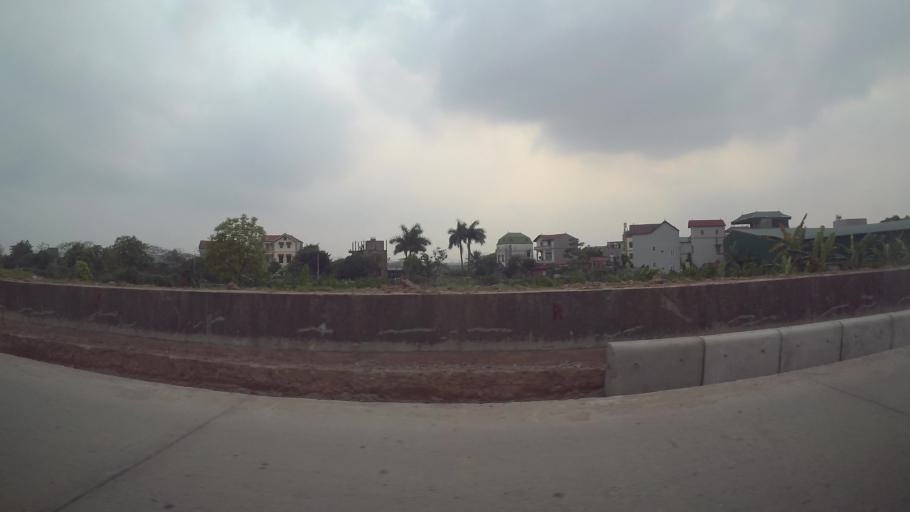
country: VN
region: Ha Noi
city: Trau Quy
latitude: 21.0096
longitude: 105.9053
